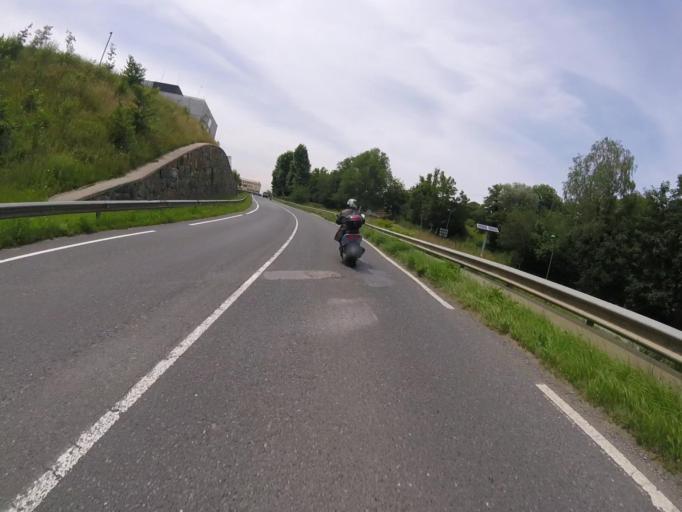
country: ES
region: Basque Country
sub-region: Provincia de Guipuzcoa
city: Hernani
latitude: 43.2762
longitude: -1.9840
